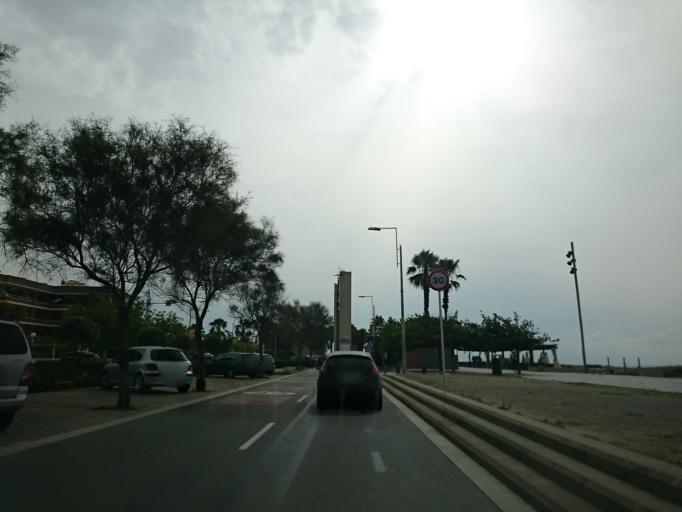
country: ES
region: Catalonia
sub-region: Provincia de Barcelona
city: Castelldefels
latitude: 41.2652
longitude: 1.9896
